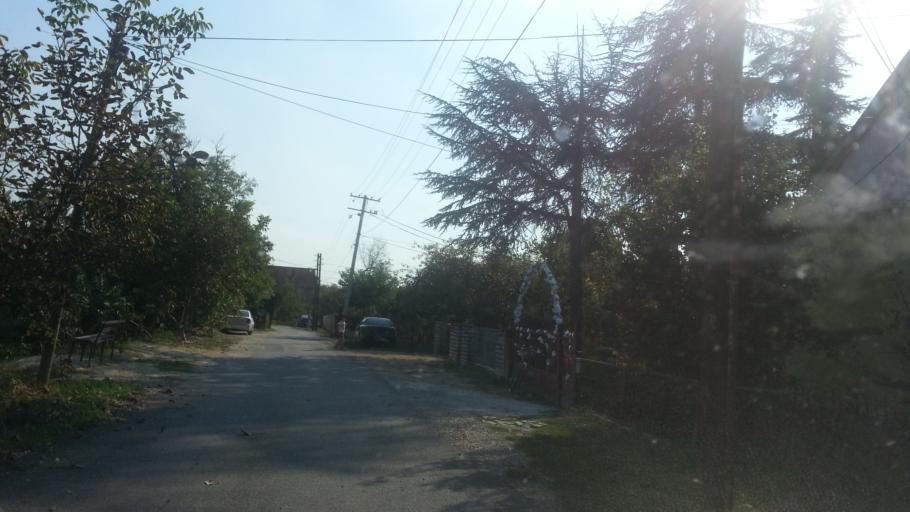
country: RS
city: Novi Banovci
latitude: 44.9583
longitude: 20.2855
